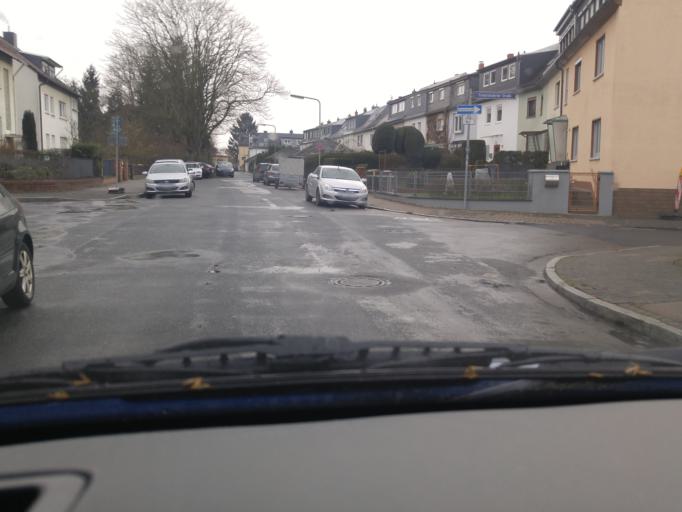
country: DE
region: Hesse
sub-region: Regierungsbezirk Darmstadt
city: Bad Homburg vor der Hoehe
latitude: 50.1851
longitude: 8.6688
